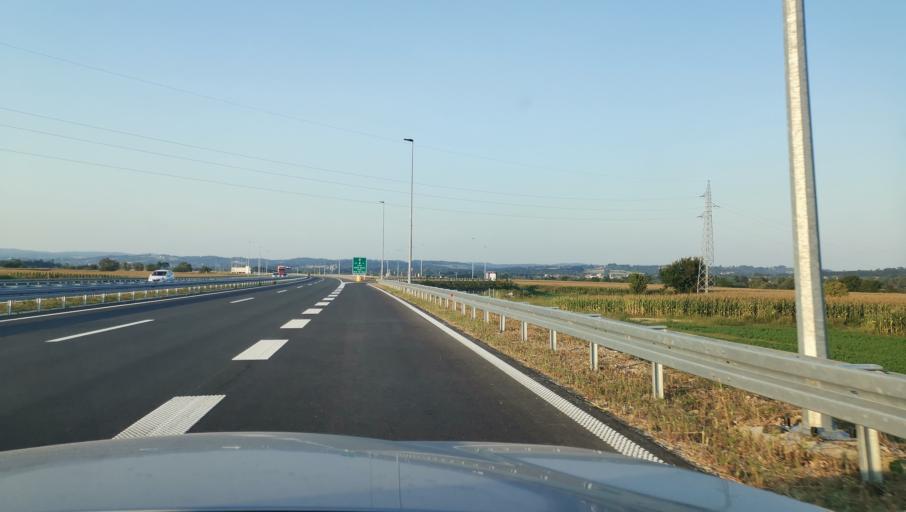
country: RS
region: Central Serbia
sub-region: Kolubarski Okrug
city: Ljig
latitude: 44.2397
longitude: 20.2605
